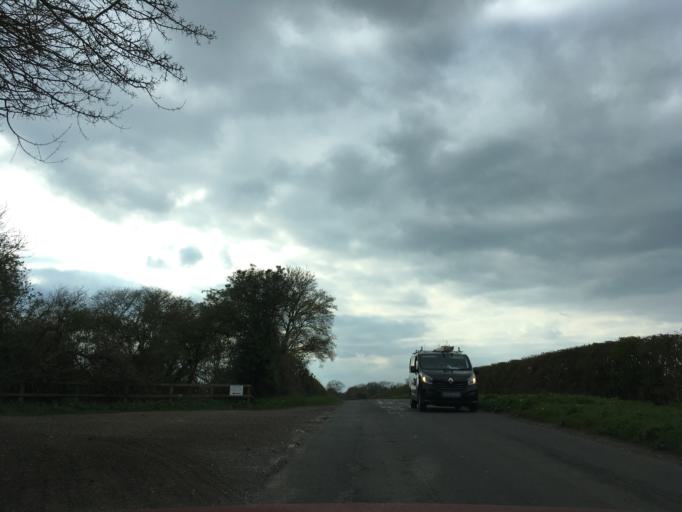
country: GB
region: England
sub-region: Oxfordshire
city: Kidlington
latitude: 51.8823
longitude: -1.2466
